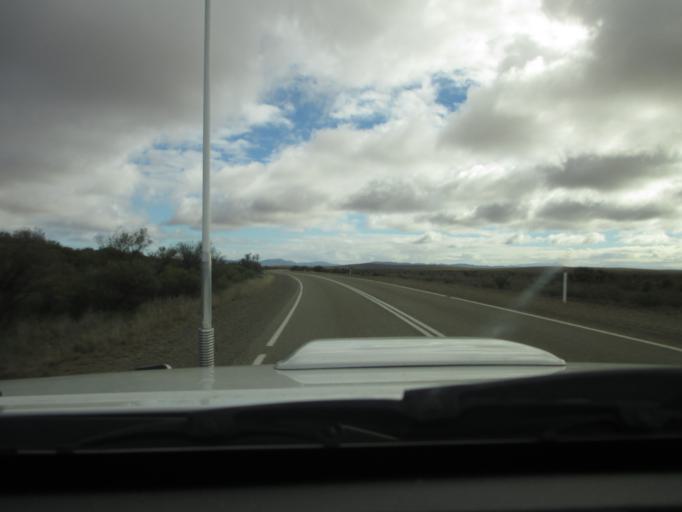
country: AU
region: South Australia
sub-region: Flinders Ranges
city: Quorn
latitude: -32.1290
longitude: 138.5118
